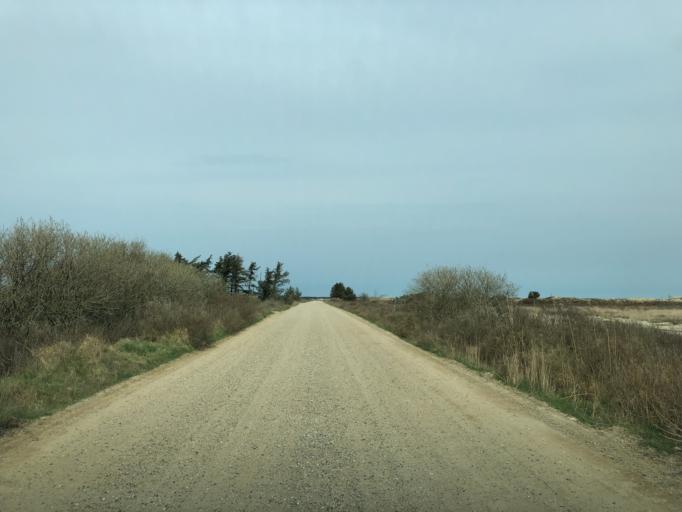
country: DK
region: South Denmark
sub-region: Varde Kommune
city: Oksbol
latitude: 55.5698
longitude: 8.1373
